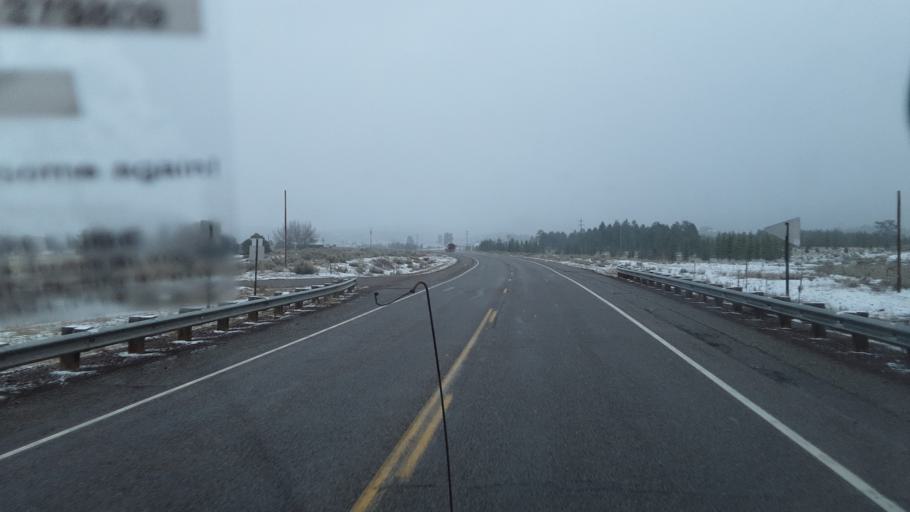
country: US
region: New Mexico
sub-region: Rio Arriba County
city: Tierra Amarilla
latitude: 36.7595
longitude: -106.5582
